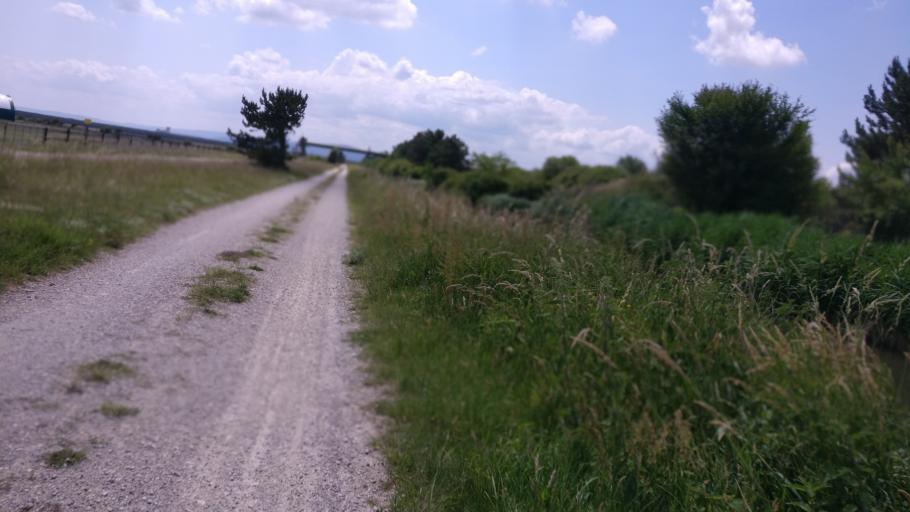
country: AT
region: Lower Austria
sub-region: Politischer Bezirk Wiener Neustadt
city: Sollenau
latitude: 47.8792
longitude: 16.2806
